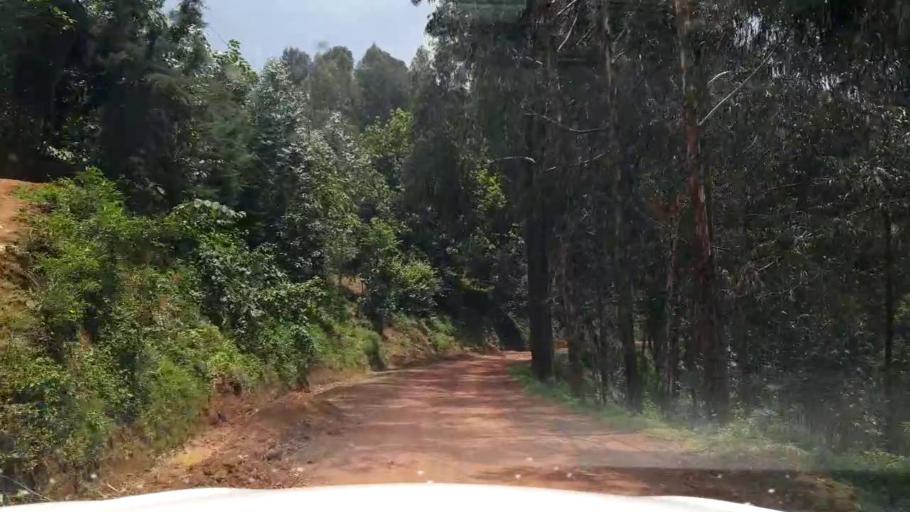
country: UG
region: Western Region
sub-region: Kabale District
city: Kabale
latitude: -1.4322
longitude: 29.8678
